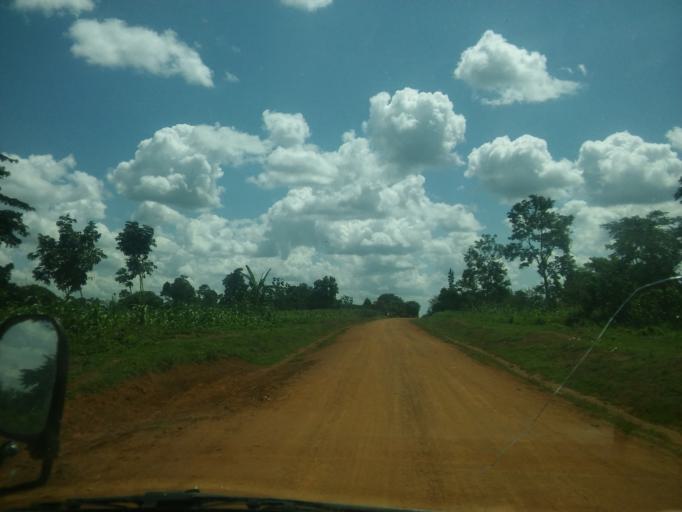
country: UG
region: Eastern Region
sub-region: Kibuku District
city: Kibuku
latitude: 1.1353
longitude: 33.8666
